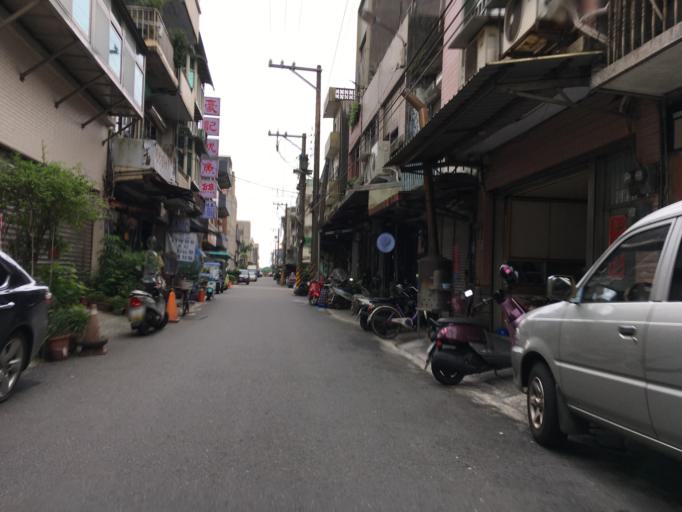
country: TW
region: Taiwan
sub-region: Yilan
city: Yilan
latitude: 24.5828
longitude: 121.8669
